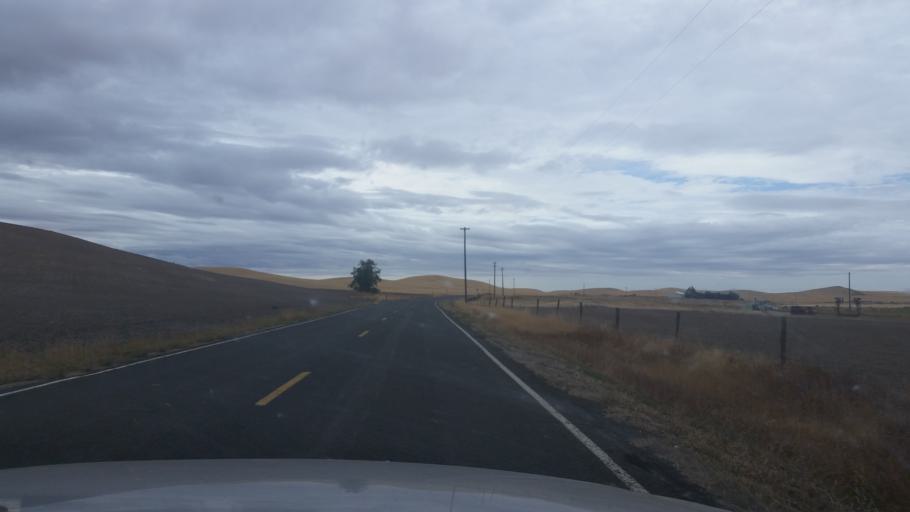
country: US
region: Washington
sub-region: Spokane County
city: Medical Lake
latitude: 47.5193
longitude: -117.8839
